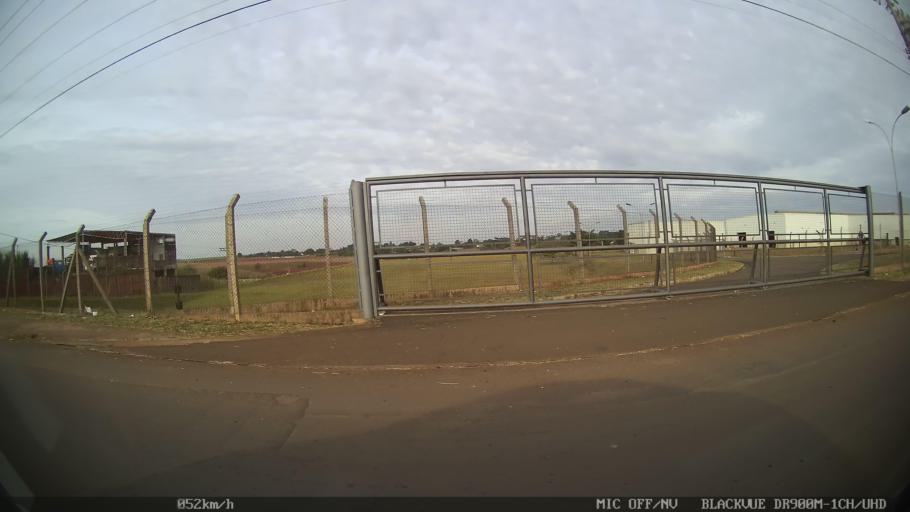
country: BR
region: Sao Paulo
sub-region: Piracicaba
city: Piracicaba
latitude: -22.7324
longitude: -47.5878
